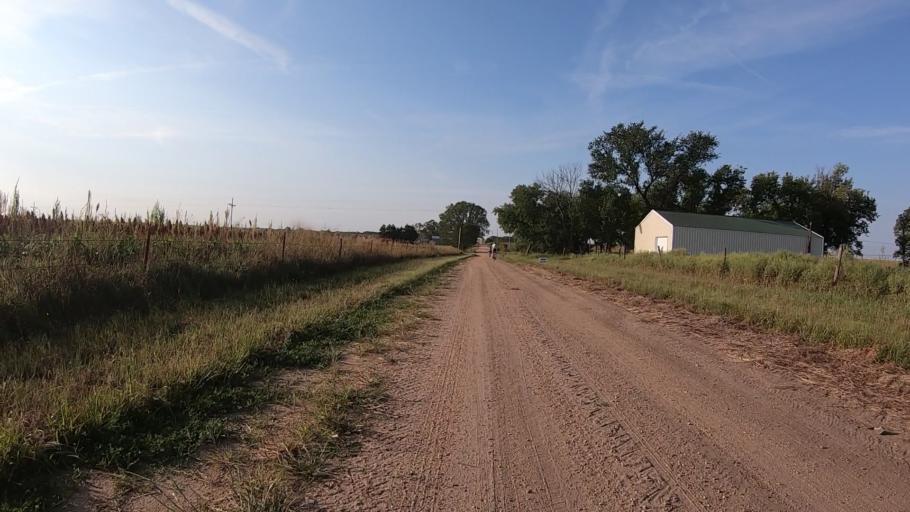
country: US
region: Kansas
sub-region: Marshall County
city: Blue Rapids
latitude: 39.7123
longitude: -96.8067
